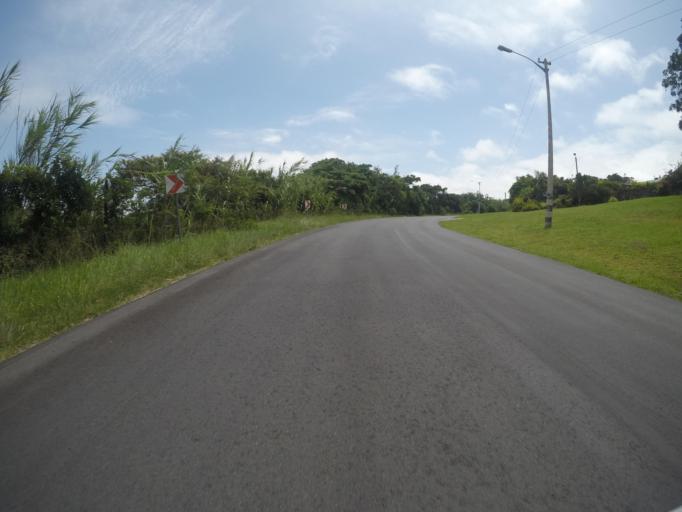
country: ZA
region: Eastern Cape
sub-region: Buffalo City Metropolitan Municipality
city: East London
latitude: -33.0004
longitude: 27.9250
